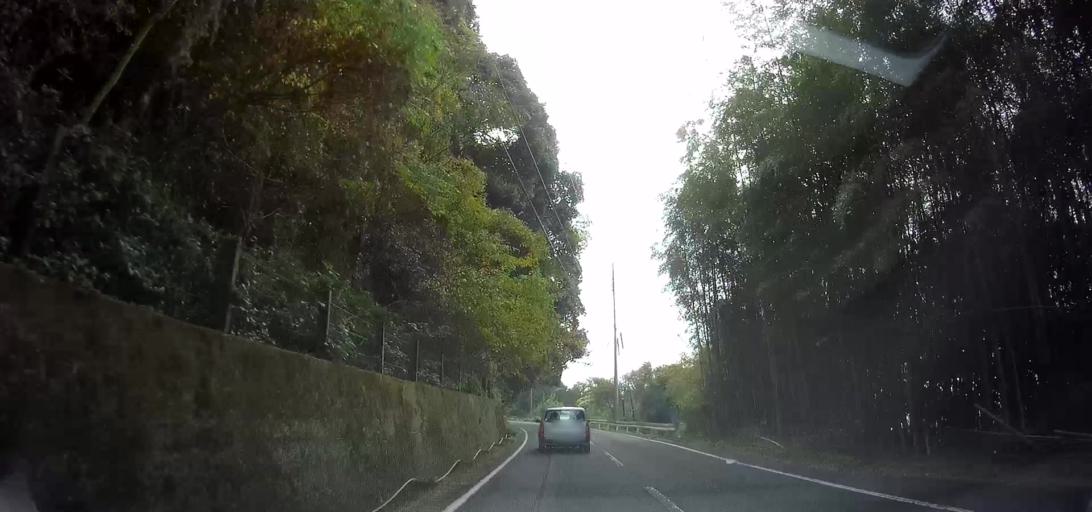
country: JP
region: Nagasaki
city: Shimabara
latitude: 32.6867
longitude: 130.2770
